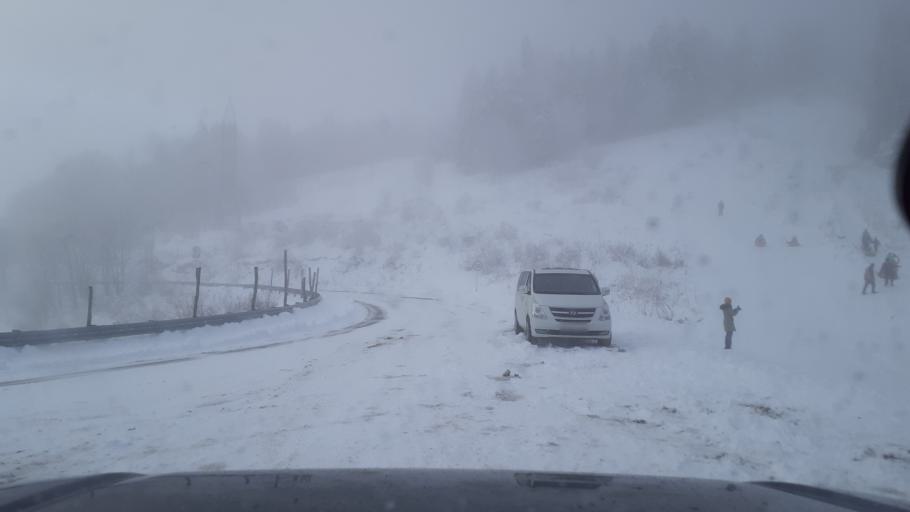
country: RU
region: Adygeya
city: Kamennomostskiy
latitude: 44.0113
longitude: 40.0342
